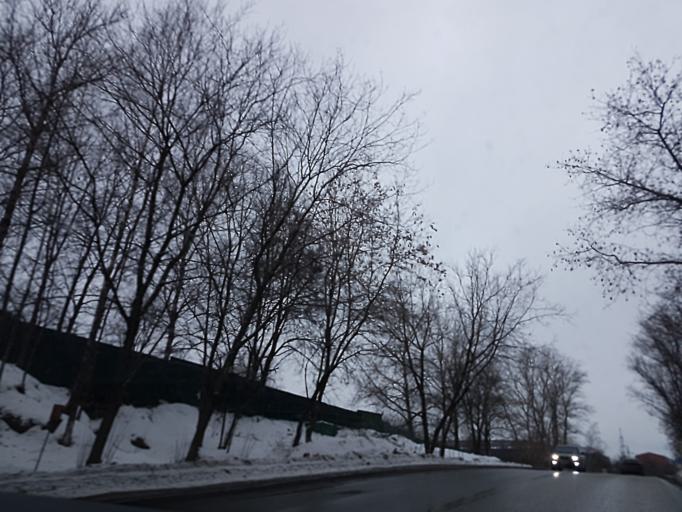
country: RU
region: Moskovskaya
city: Pavshino
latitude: 55.8214
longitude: 37.3577
